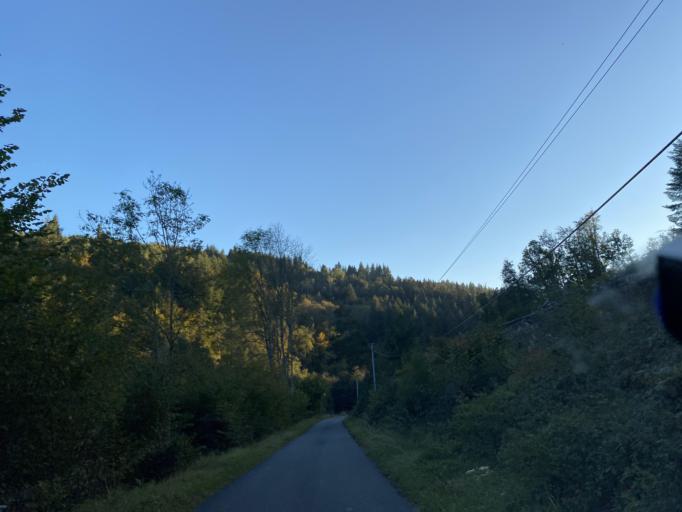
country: FR
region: Rhone-Alpes
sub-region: Departement de la Loire
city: Saint-Just-en-Chevalet
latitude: 45.9338
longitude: 3.8565
